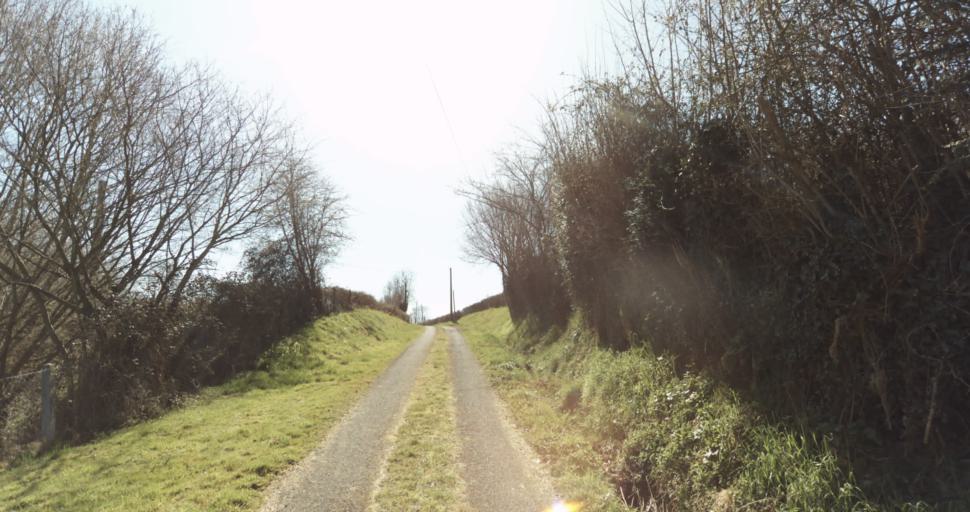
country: FR
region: Lower Normandy
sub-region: Departement du Calvados
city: Livarot
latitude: 49.0097
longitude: 0.0873
